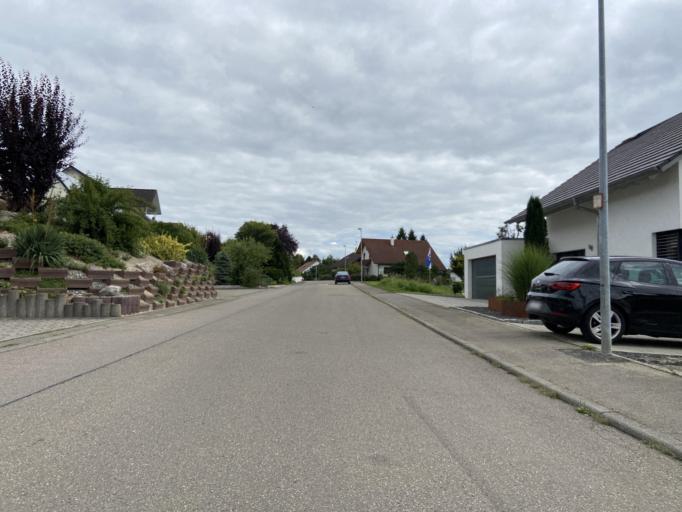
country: DE
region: Baden-Wuerttemberg
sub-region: Tuebingen Region
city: Sigmaringendorf
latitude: 48.0726
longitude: 9.2587
